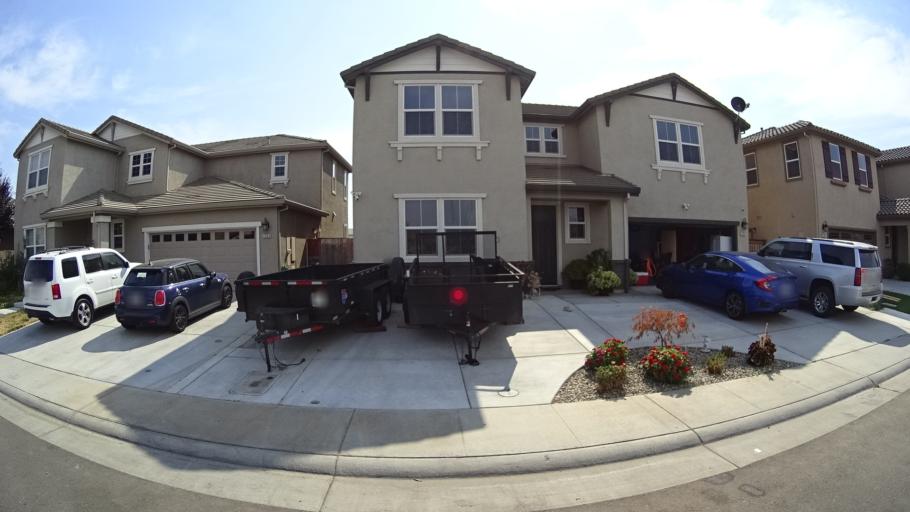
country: US
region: California
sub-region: Sacramento County
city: Laguna
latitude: 38.3739
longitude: -121.4463
